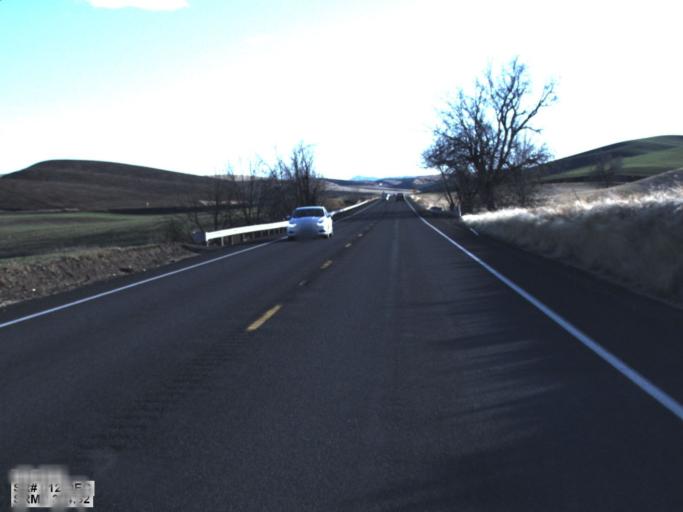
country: US
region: Washington
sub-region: Walla Walla County
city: Waitsburg
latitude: 46.2279
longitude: -118.1375
